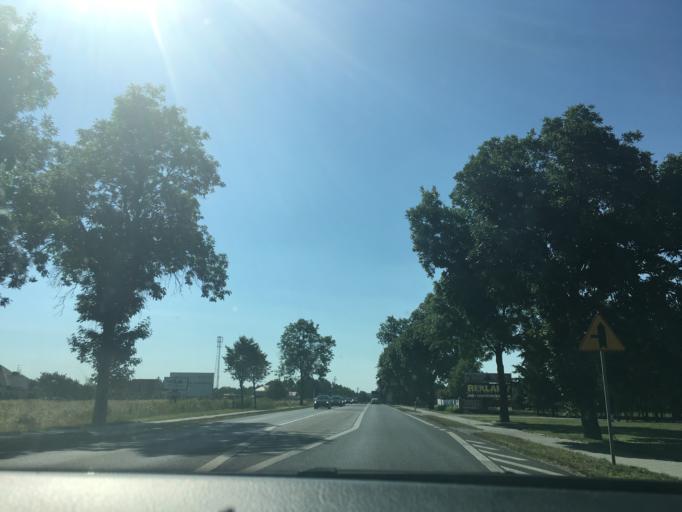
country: PL
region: Lublin Voivodeship
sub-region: Powiat lubartowski
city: Serniki
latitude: 51.4253
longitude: 22.6373
